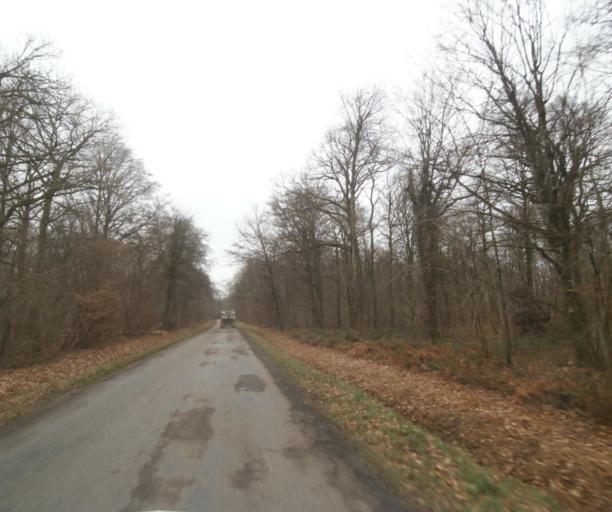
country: FR
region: Champagne-Ardenne
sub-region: Departement de la Haute-Marne
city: Wassy
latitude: 48.5259
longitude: 4.9761
